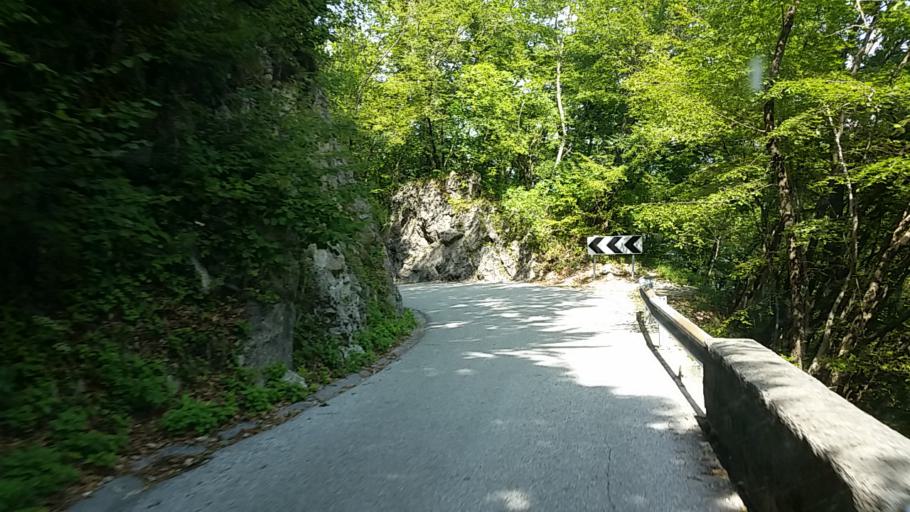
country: SI
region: Tolmin
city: Tolmin
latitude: 46.1095
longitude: 13.8028
